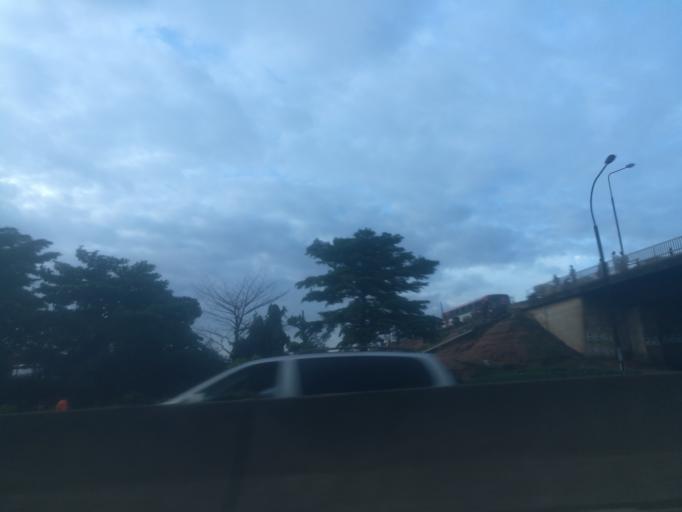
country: NG
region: Lagos
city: Somolu
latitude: 6.5501
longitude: 3.3926
